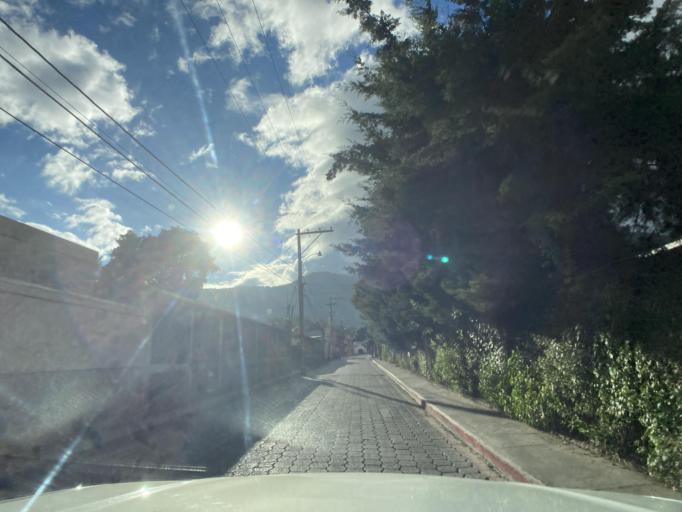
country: GT
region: Sacatepequez
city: Jocotenango
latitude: 14.5746
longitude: -90.7432
